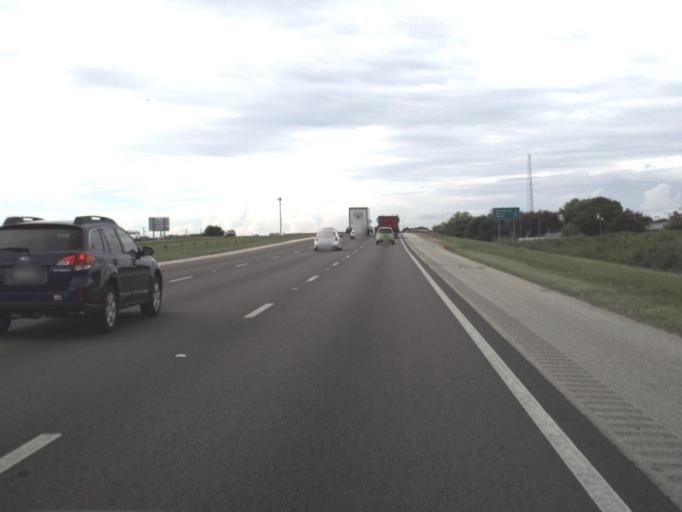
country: US
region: Florida
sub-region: Sarasota County
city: Fruitville
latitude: 27.3291
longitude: -82.4477
